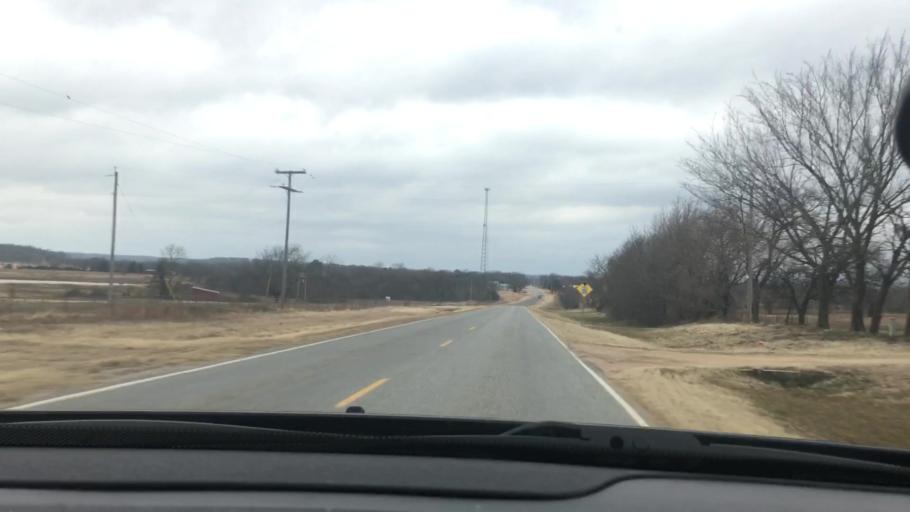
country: US
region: Oklahoma
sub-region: Coal County
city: Coalgate
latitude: 34.3749
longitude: -96.4076
